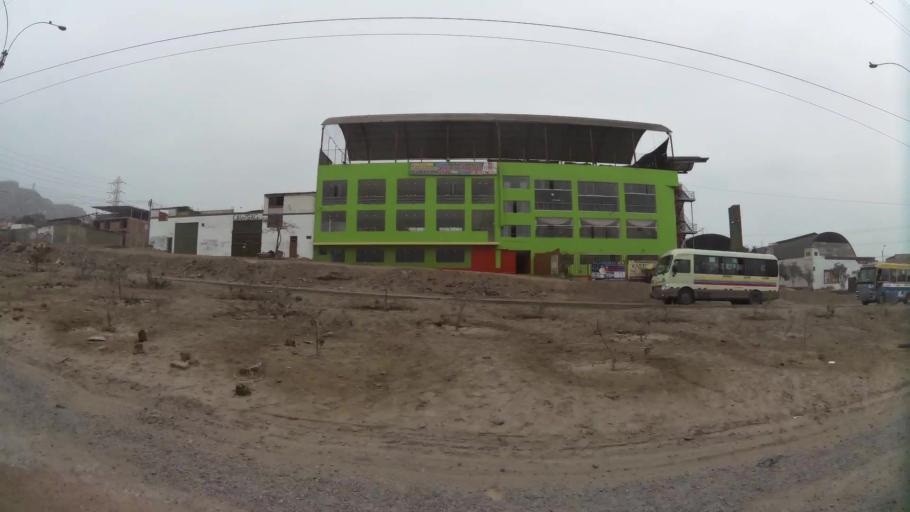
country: PE
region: Lima
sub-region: Lima
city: Surco
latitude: -12.1833
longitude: -76.9438
